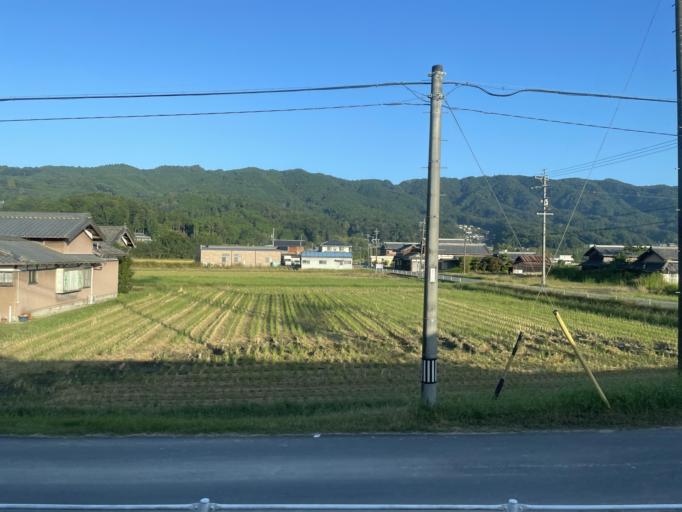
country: JP
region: Mie
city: Nabari
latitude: 34.5929
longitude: 136.0656
